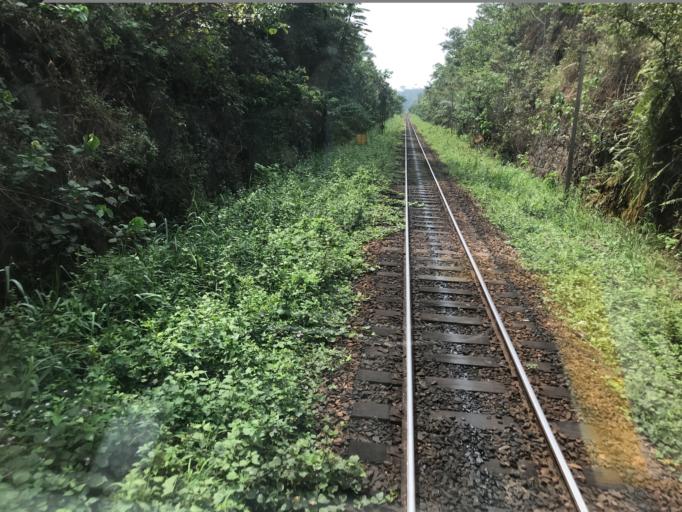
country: CM
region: Centre
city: Eseka
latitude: 3.5809
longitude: 10.8961
